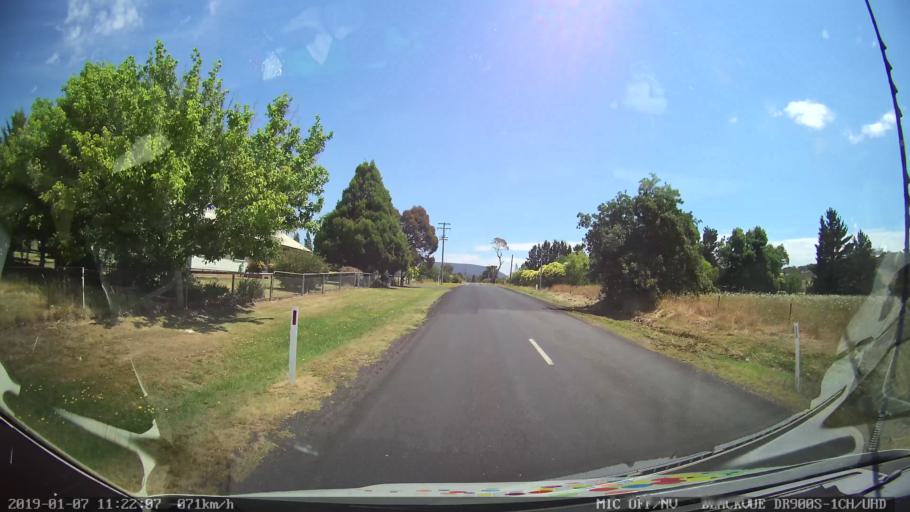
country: AU
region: New South Wales
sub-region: Armidale Dumaresq
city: Armidale
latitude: -30.4866
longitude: 151.6277
